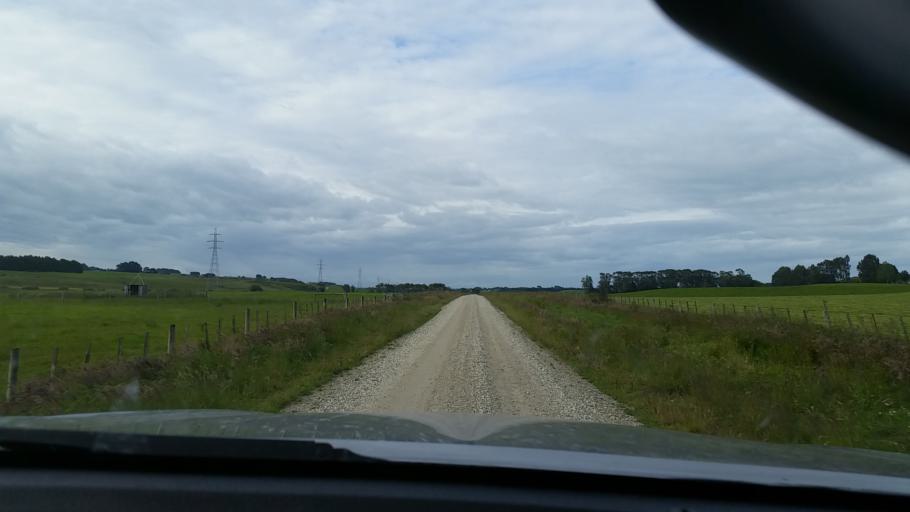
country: NZ
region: Southland
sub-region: Gore District
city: Gore
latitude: -46.2166
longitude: 168.7541
